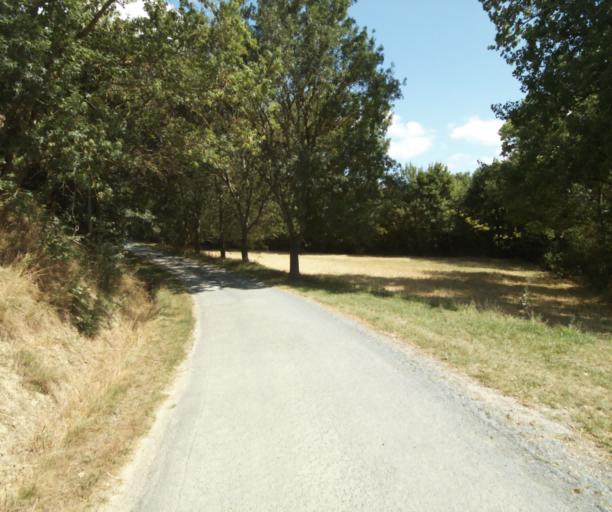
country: FR
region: Midi-Pyrenees
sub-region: Departement de la Haute-Garonne
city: Auriac-sur-Vendinelle
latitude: 43.4799
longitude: 1.8456
